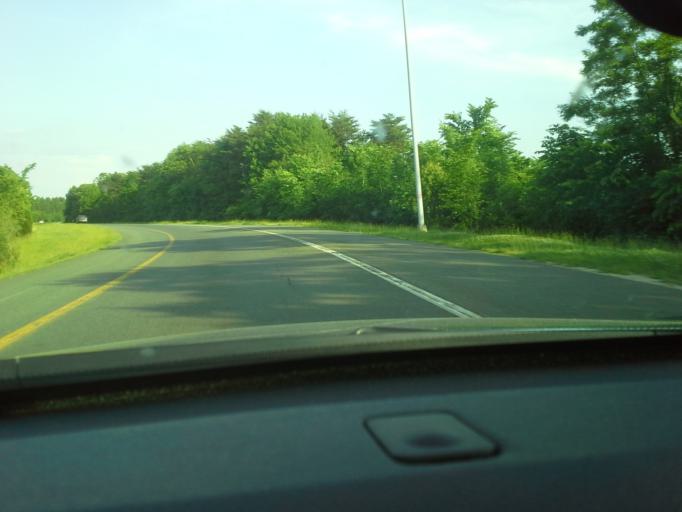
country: US
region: Maryland
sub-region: Anne Arundel County
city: Glen Burnie
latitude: 39.1523
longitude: -76.6489
